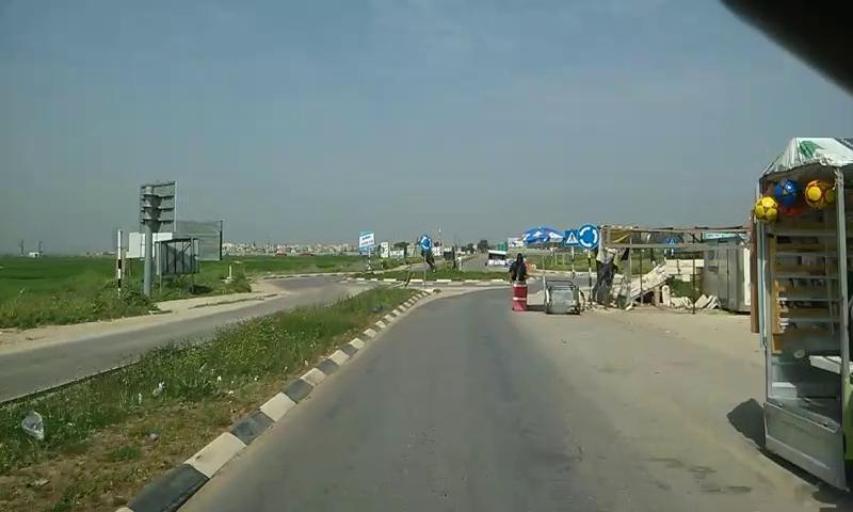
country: PS
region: West Bank
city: Al Jalamah
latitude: 32.4991
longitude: 35.3019
